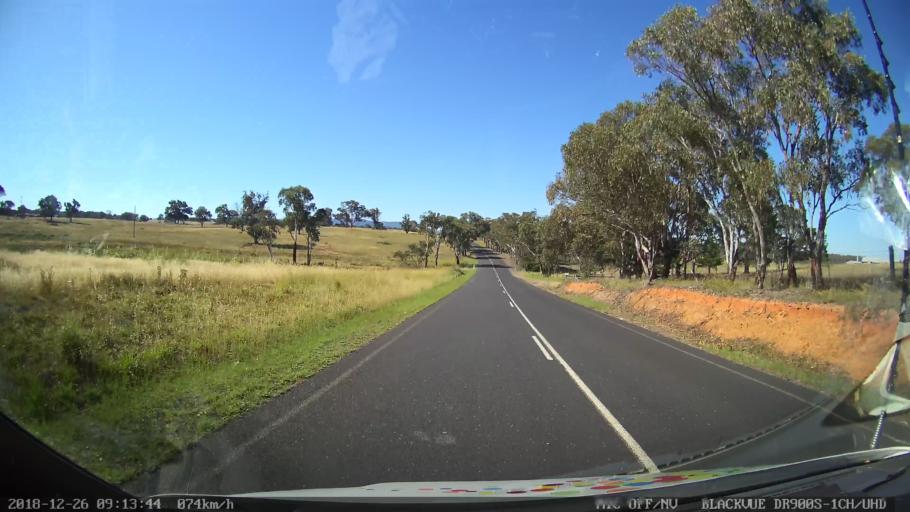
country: AU
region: New South Wales
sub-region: Mid-Western Regional
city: Kandos
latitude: -32.7708
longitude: 149.9804
